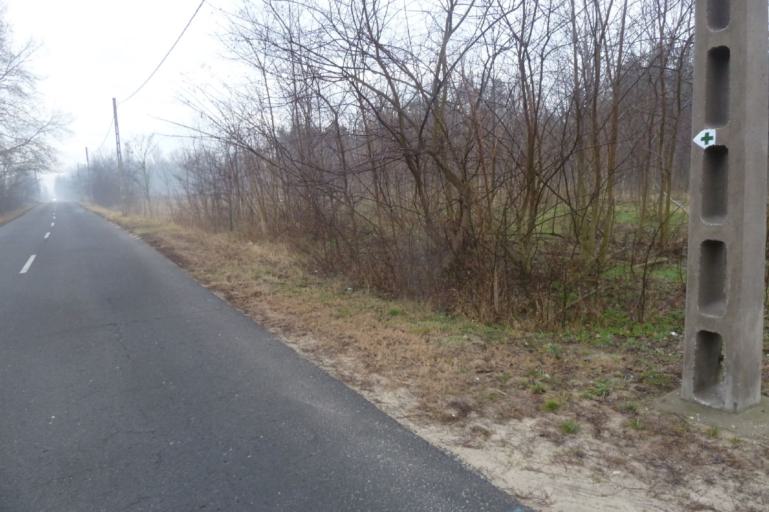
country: HU
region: Pest
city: Tapioszentmarton
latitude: 47.3566
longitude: 19.7934
